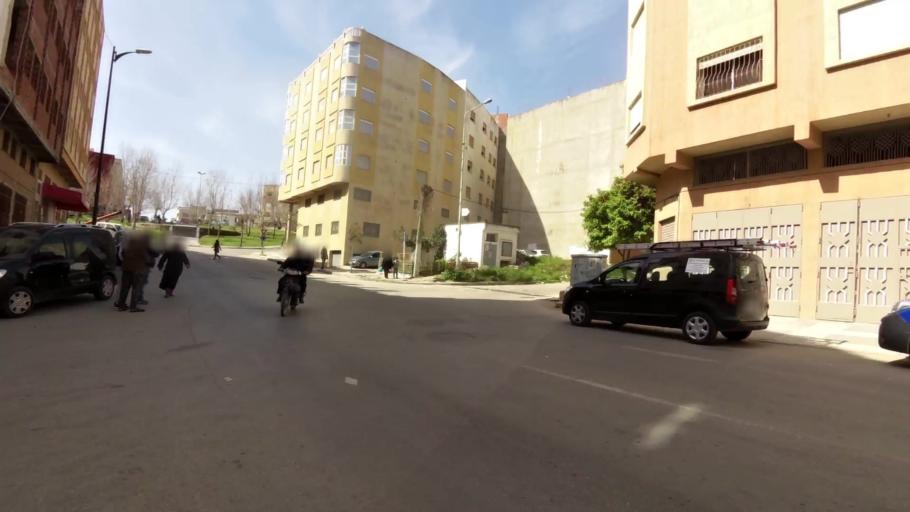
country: MA
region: Tanger-Tetouan
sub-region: Tanger-Assilah
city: Tangier
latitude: 35.7326
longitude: -5.8057
